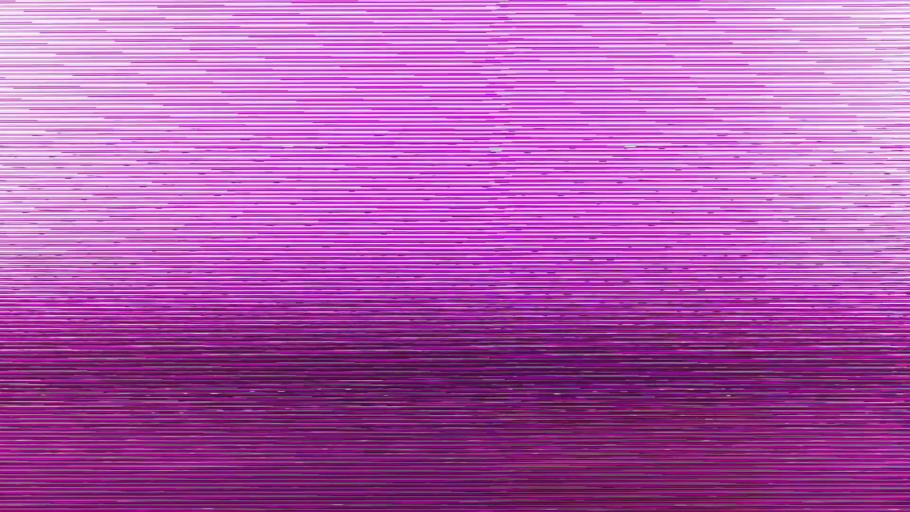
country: US
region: Michigan
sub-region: Wayne County
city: Garden City
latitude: 42.3391
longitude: -83.3507
